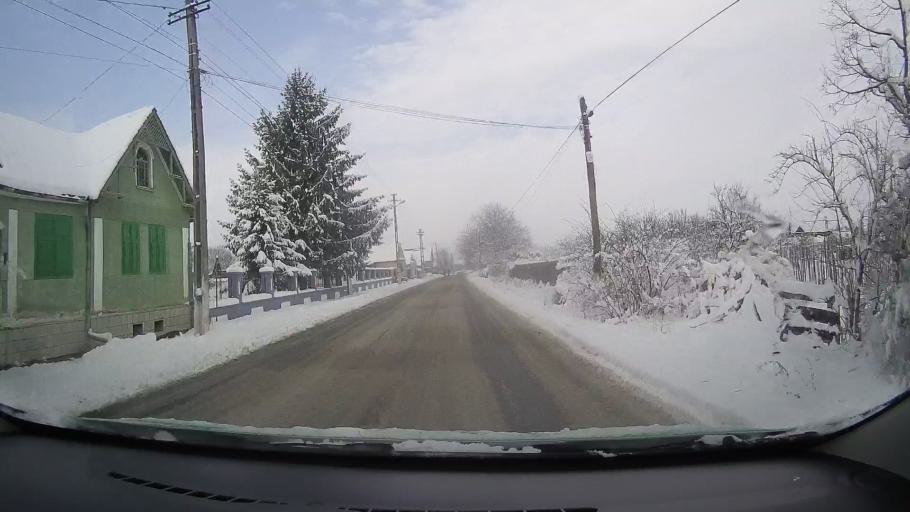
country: RO
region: Alba
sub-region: Comuna Pianu
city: Pianu de Jos
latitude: 45.9415
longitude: 23.4835
